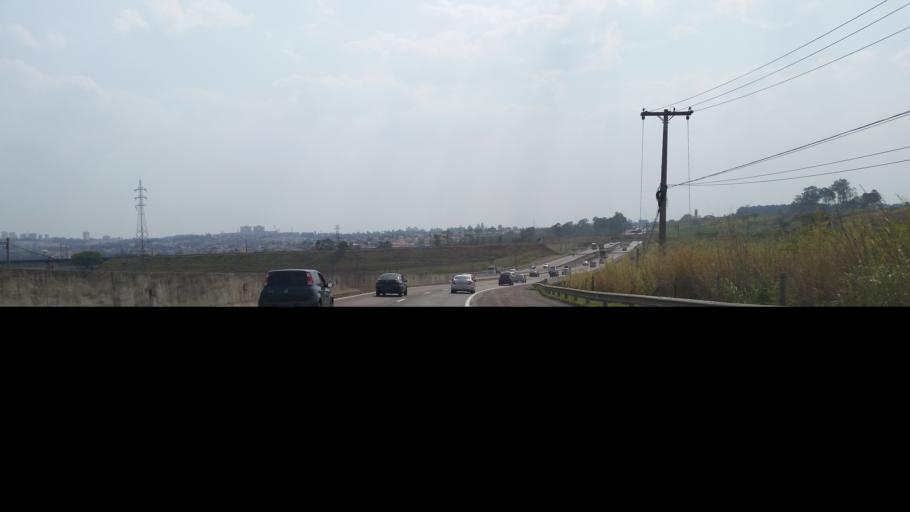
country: BR
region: Sao Paulo
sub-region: Campinas
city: Campinas
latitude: -22.8919
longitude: -47.1355
